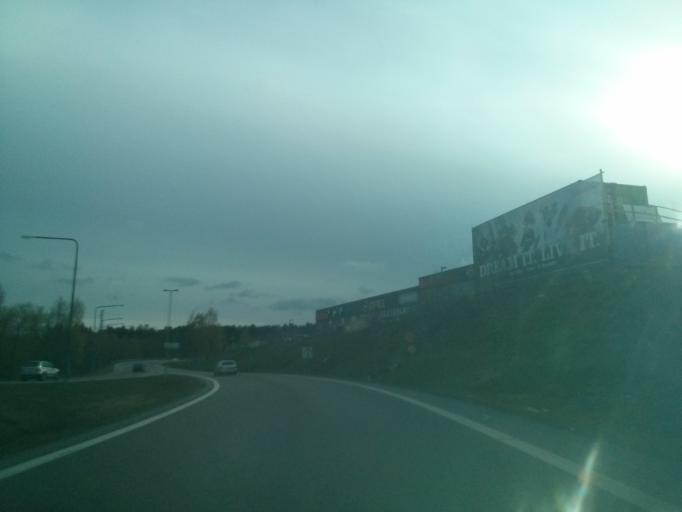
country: SE
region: Vaesternorrland
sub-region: Sundsvalls Kommun
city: Sundsvall
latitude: 62.4126
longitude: 17.3381
